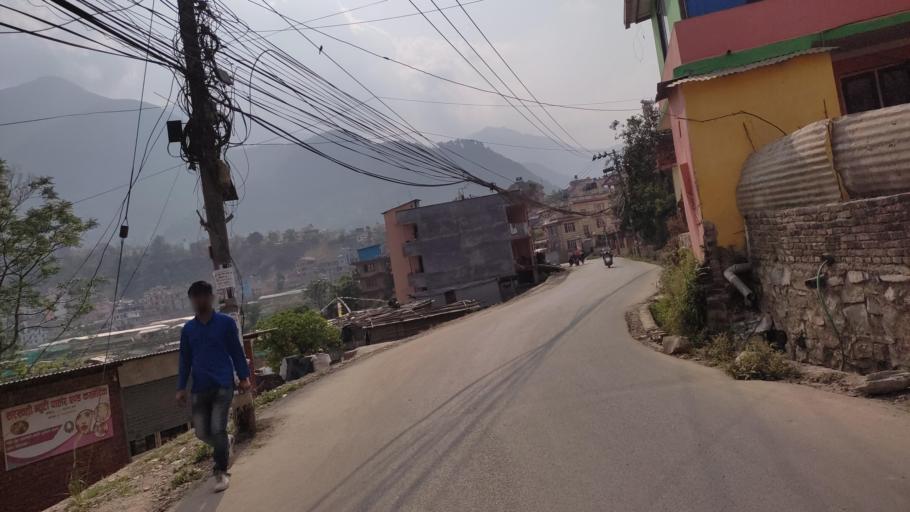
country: NP
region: Central Region
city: Kirtipur
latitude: 27.6665
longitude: 85.2618
